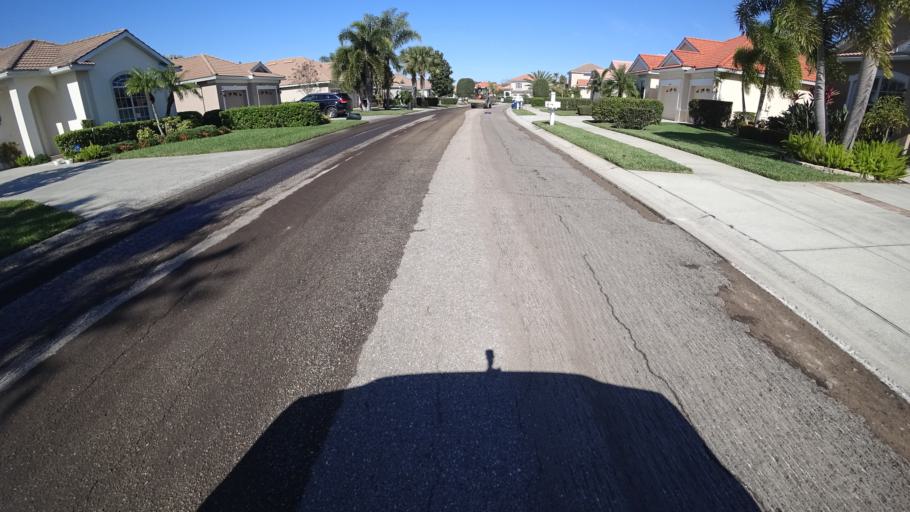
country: US
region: Florida
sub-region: Sarasota County
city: Desoto Lakes
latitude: 27.4264
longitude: -82.4647
